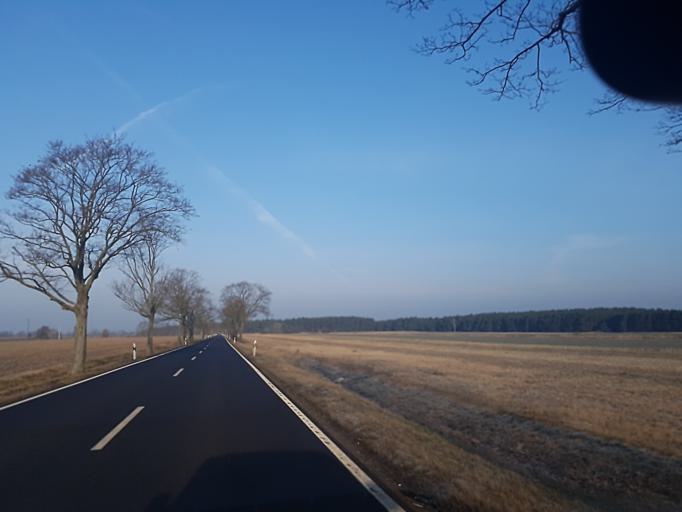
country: DE
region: Brandenburg
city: Golzow
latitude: 52.2653
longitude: 12.6533
